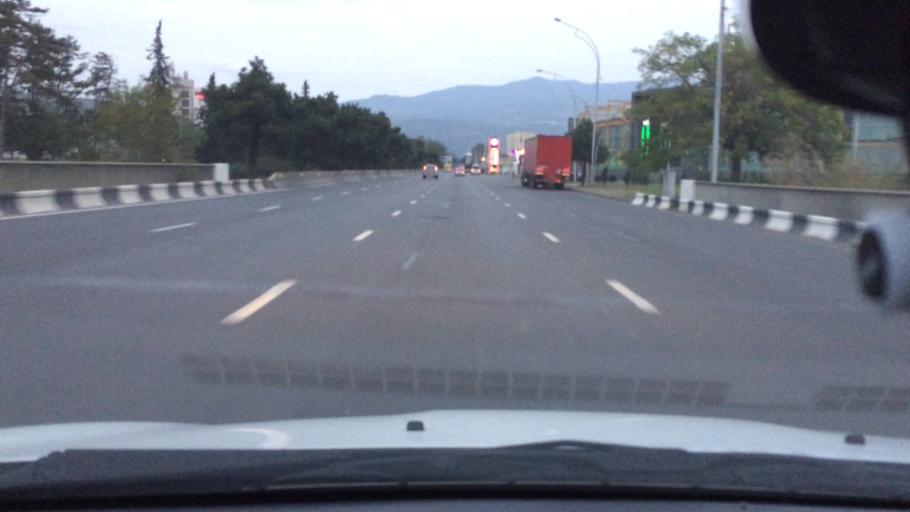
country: GE
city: Zahesi
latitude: 41.7871
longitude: 44.7701
